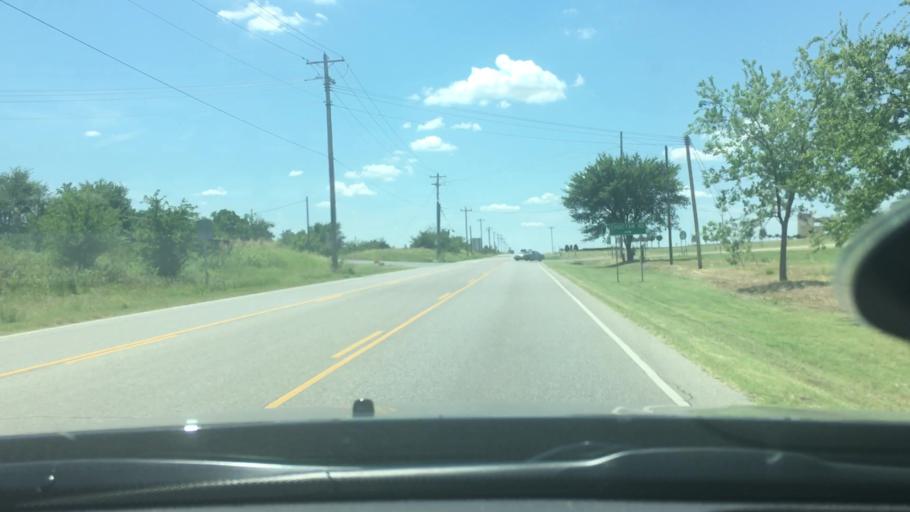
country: US
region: Oklahoma
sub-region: Bryan County
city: Calera
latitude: 33.9549
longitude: -96.4056
